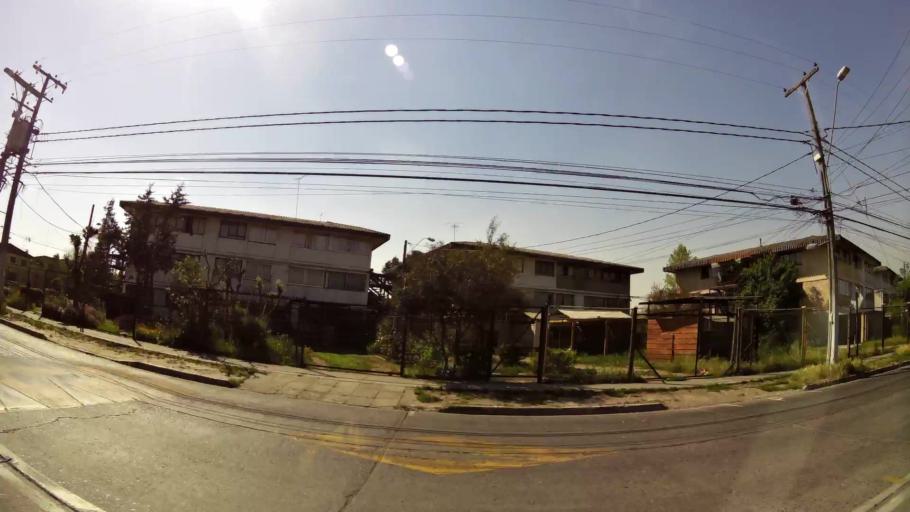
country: CL
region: Santiago Metropolitan
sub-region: Provincia de Santiago
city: La Pintana
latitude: -33.5430
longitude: -70.5979
